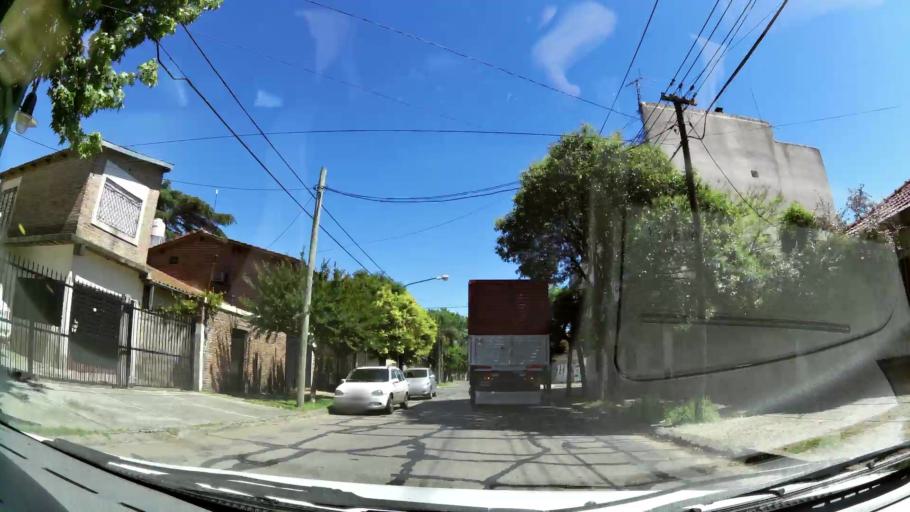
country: AR
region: Buenos Aires
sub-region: Partido de General San Martin
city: General San Martin
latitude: -34.5273
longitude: -58.5460
